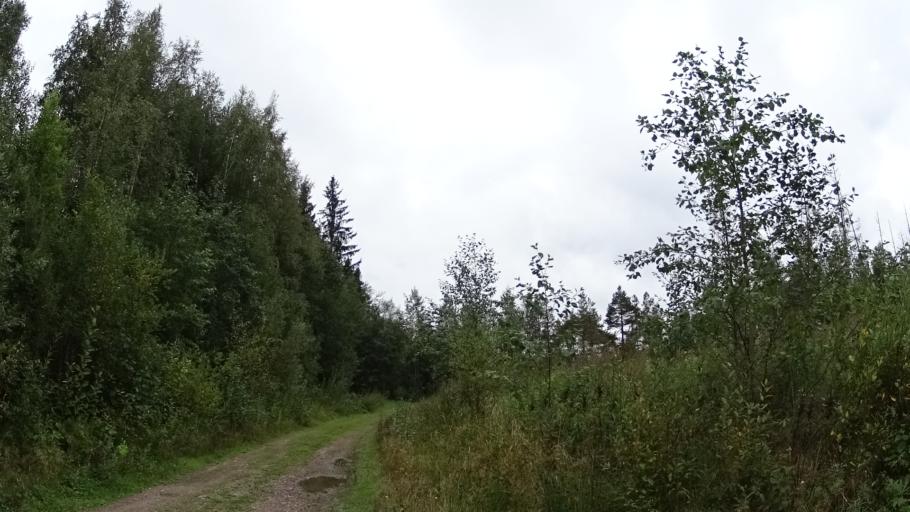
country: FI
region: Uusimaa
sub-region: Helsinki
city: Kilo
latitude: 60.3225
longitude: 24.8223
